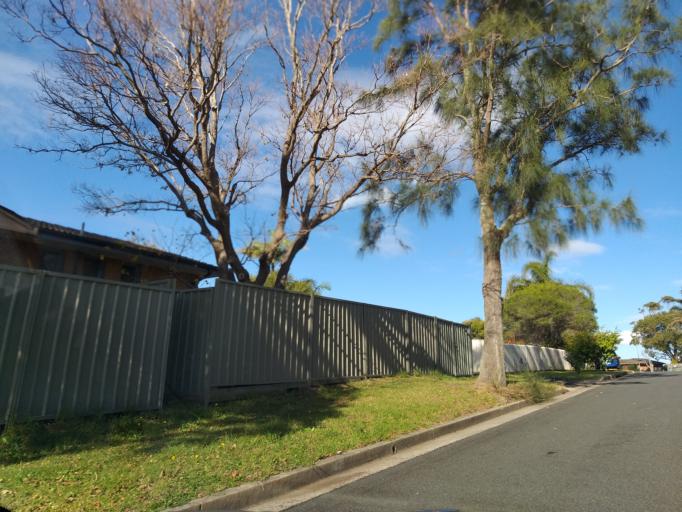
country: AU
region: New South Wales
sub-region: Wollongong
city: East Corrimal
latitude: -34.3655
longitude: 150.9183
